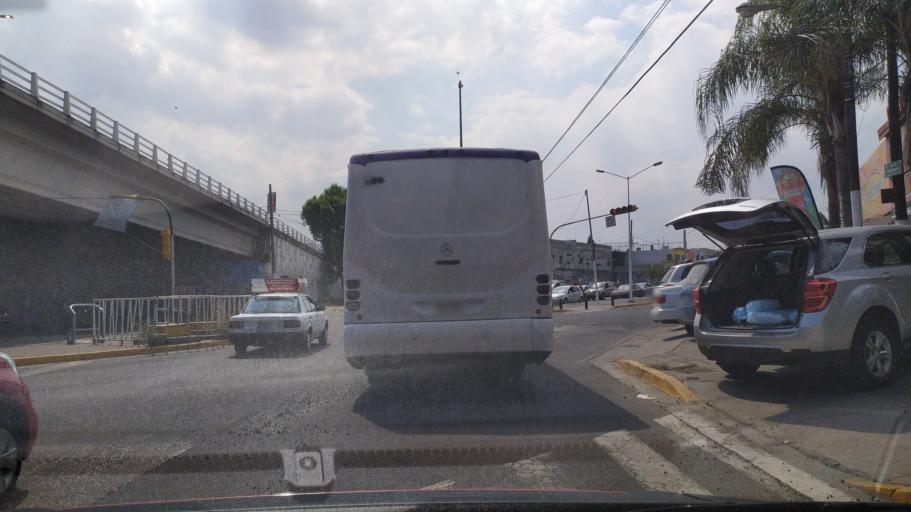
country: MX
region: Jalisco
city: Zapopan2
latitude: 20.7311
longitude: -103.4129
